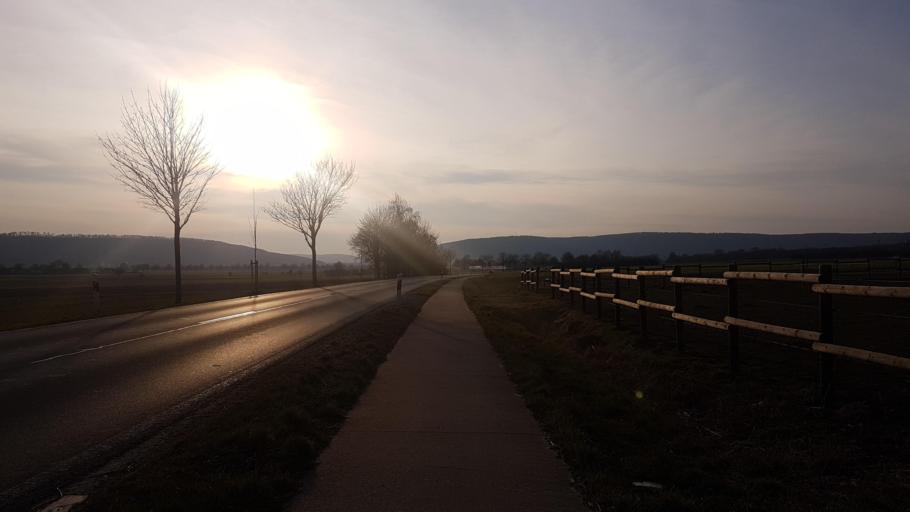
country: DE
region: Lower Saxony
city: Springe
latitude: 52.2108
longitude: 9.6134
